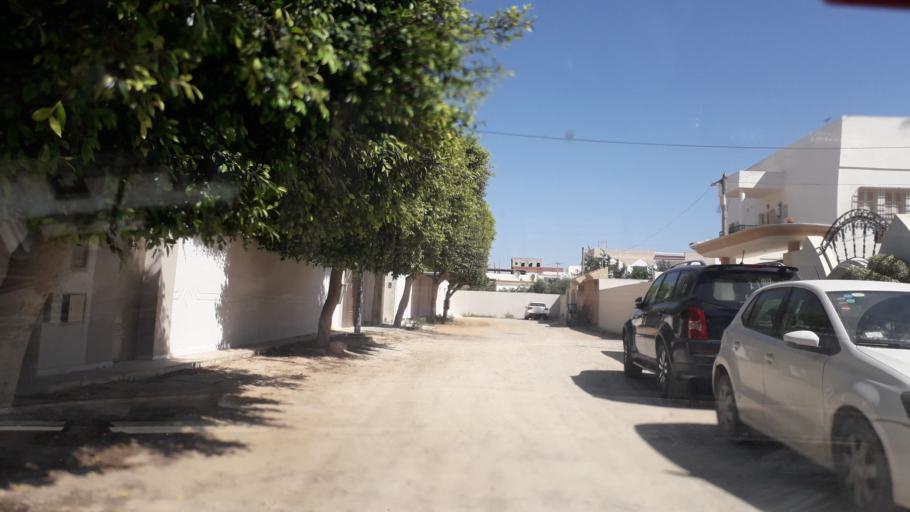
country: TN
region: Safaqis
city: Al Qarmadah
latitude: 34.8093
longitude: 10.7643
